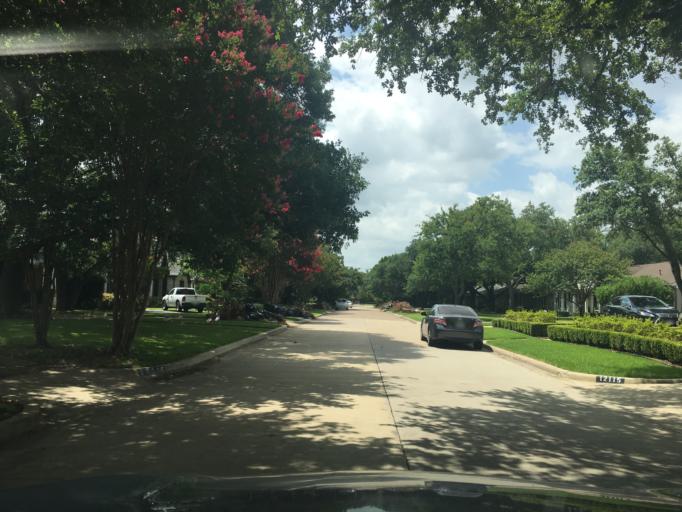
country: US
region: Texas
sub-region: Dallas County
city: Addison
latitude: 32.9137
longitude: -96.8234
